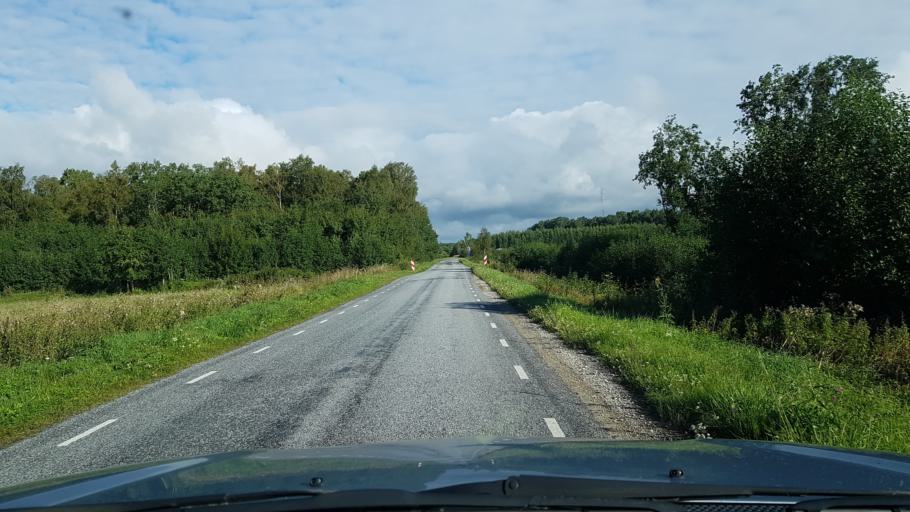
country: EE
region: Harju
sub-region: Rae vald
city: Vaida
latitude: 59.3069
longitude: 24.9257
